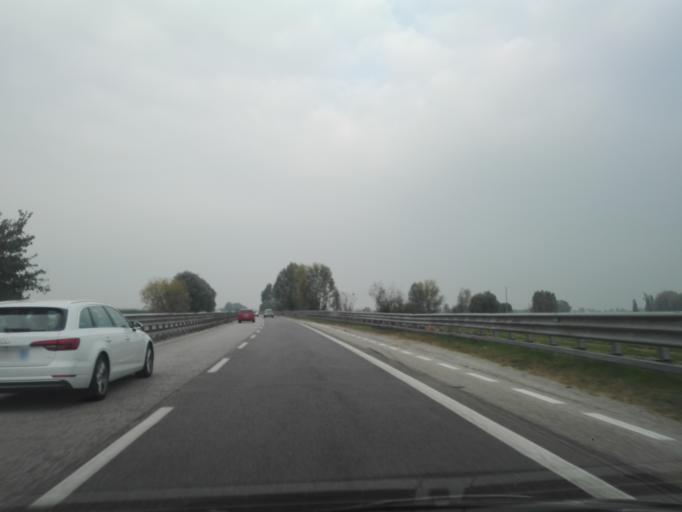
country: IT
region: Veneto
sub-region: Provincia di Verona
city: Villa Bartolomea
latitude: 45.1500
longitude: 11.3409
